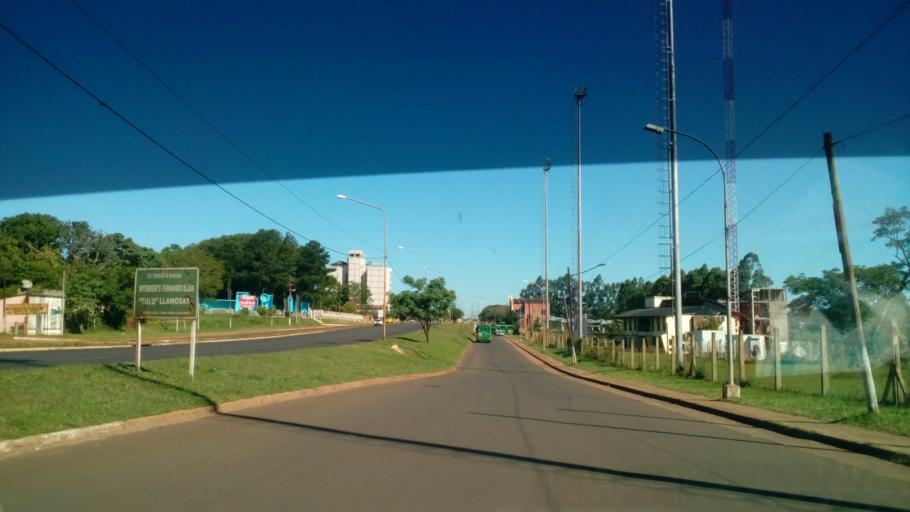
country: AR
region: Misiones
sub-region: Departamento de Capital
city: Posadas
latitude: -27.4300
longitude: -55.8905
